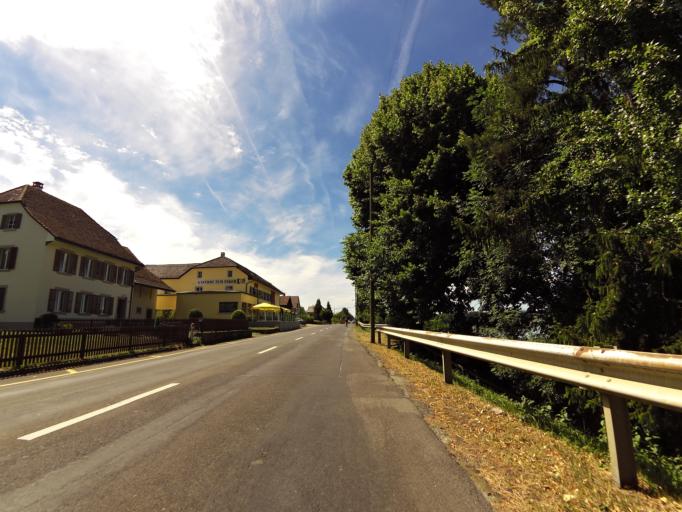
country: CH
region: Aargau
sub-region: Bezirk Rheinfelden
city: Mumpf
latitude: 47.5468
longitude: 7.9170
